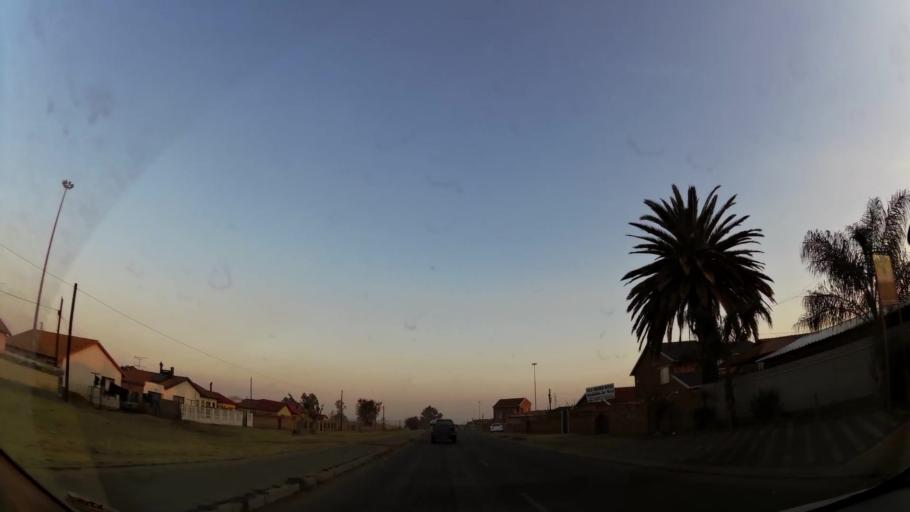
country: ZA
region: Gauteng
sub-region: Ekurhuleni Metropolitan Municipality
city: Springs
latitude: -26.3004
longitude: 28.4073
